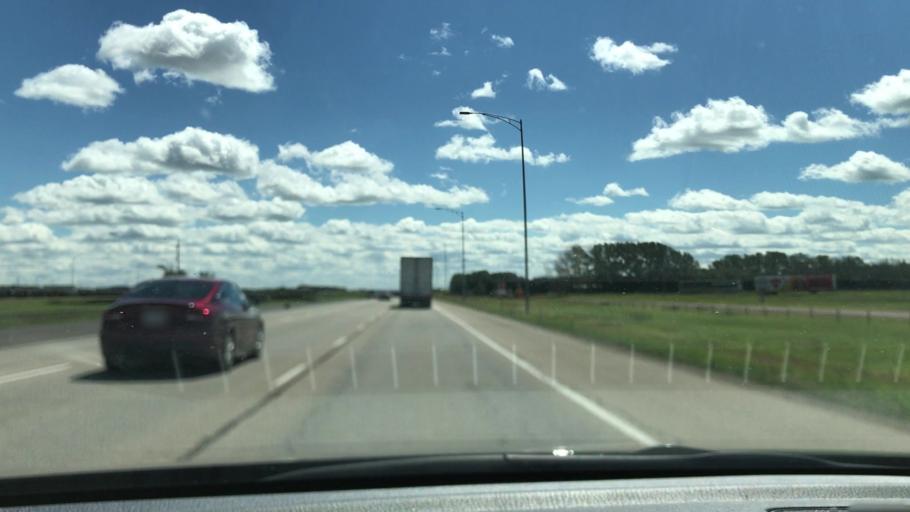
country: CA
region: Alberta
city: Leduc
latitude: 53.3692
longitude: -113.5289
